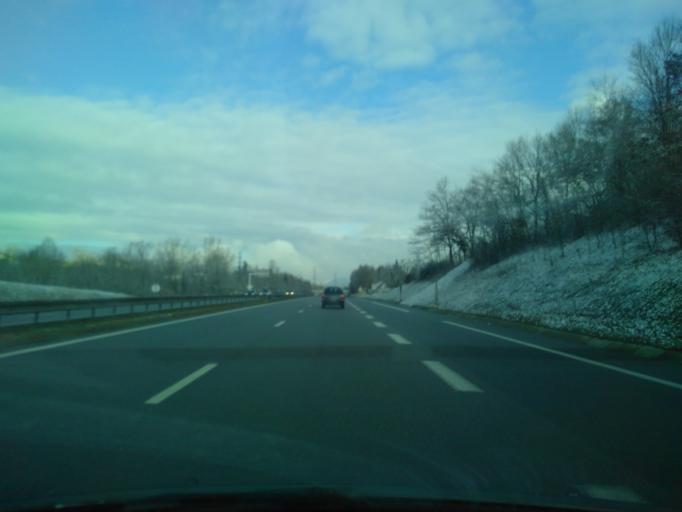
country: FR
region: Rhone-Alpes
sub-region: Departement de la Haute-Savoie
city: Viuz-la-Chiesaz
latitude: 45.8505
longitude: 6.0567
